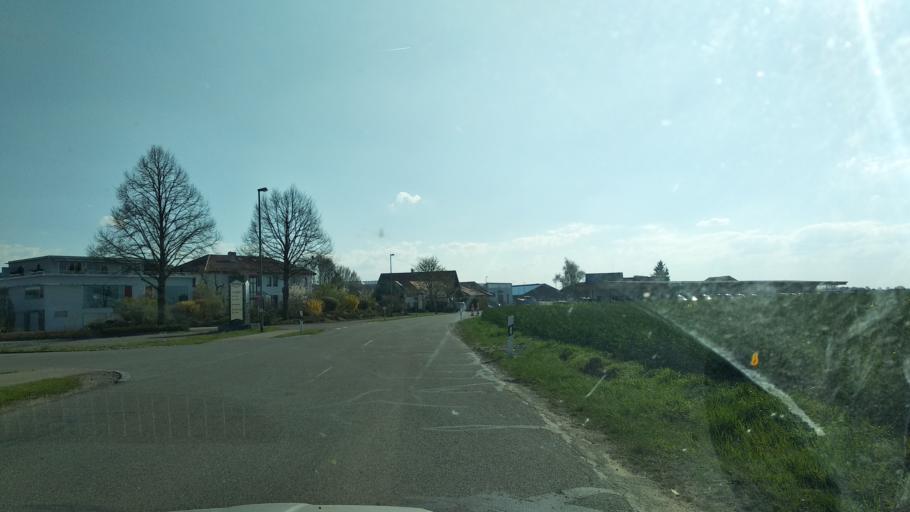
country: DE
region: Bavaria
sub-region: Swabia
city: Hawangen
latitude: 47.9684
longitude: 10.2576
